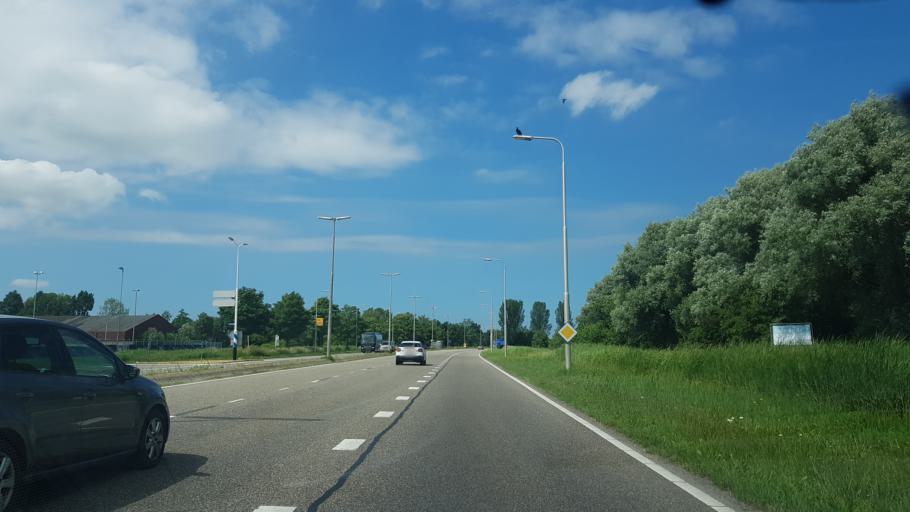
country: NL
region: Friesland
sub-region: Gemeente Leeuwarden
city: Camminghaburen
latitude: 53.2116
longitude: 5.8309
